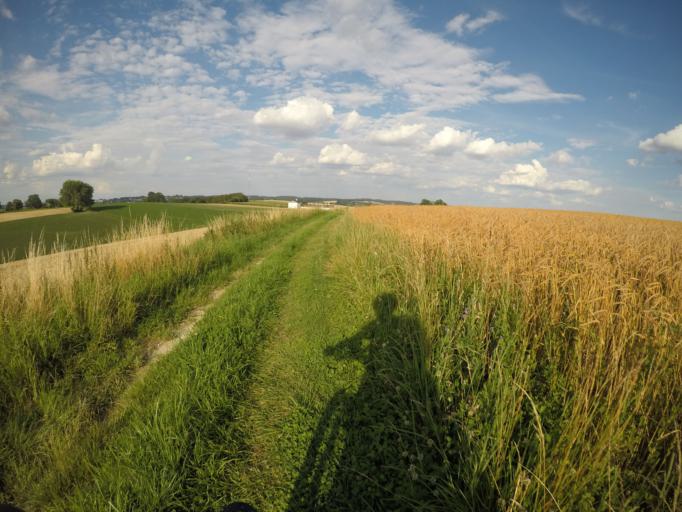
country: DE
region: Bavaria
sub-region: Lower Bavaria
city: Tiefenbach
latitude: 48.5081
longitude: 12.1228
